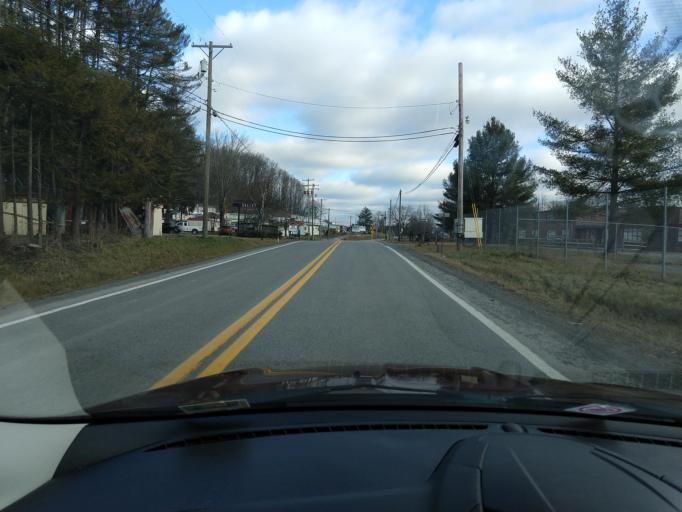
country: US
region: West Virginia
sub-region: Randolph County
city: Elkins
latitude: 38.7882
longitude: -79.9055
